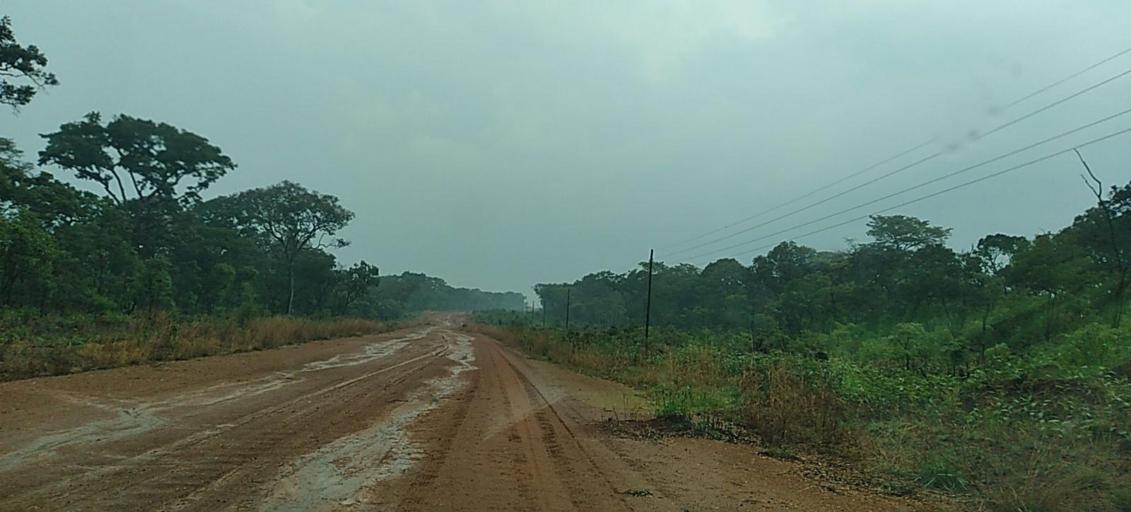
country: ZM
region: North-Western
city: Mwinilunga
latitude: -11.5952
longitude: 24.3903
